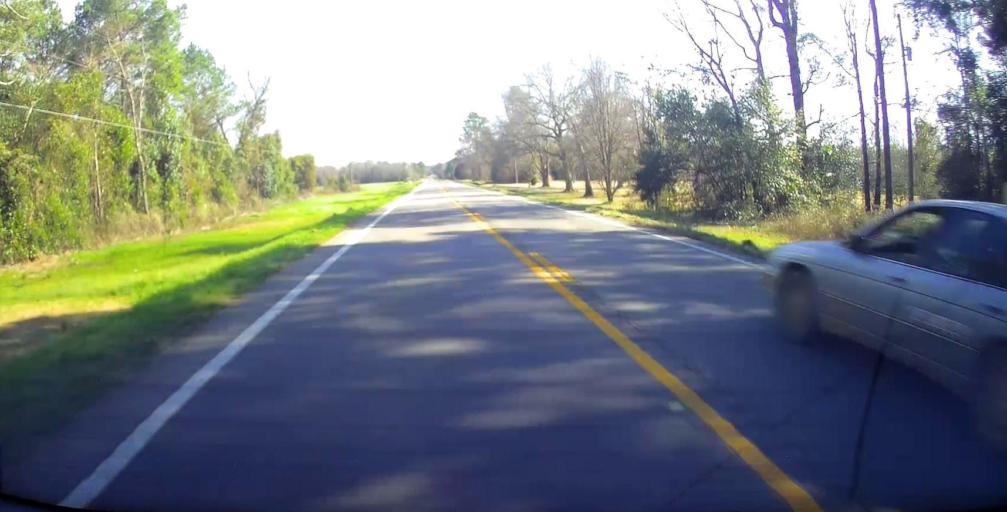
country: US
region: Georgia
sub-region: Macon County
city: Oglethorpe
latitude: 32.3262
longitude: -84.0712
